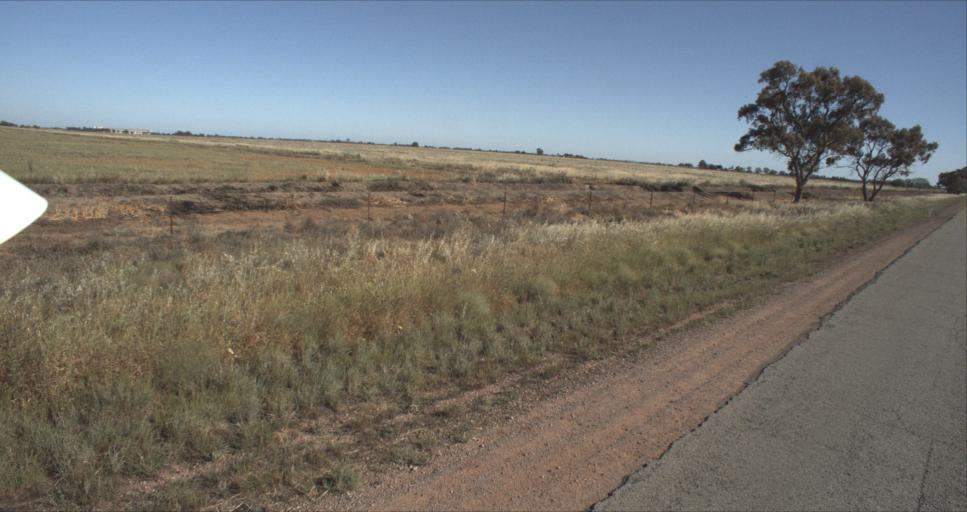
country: AU
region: New South Wales
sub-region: Leeton
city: Leeton
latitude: -34.5636
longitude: 146.3122
